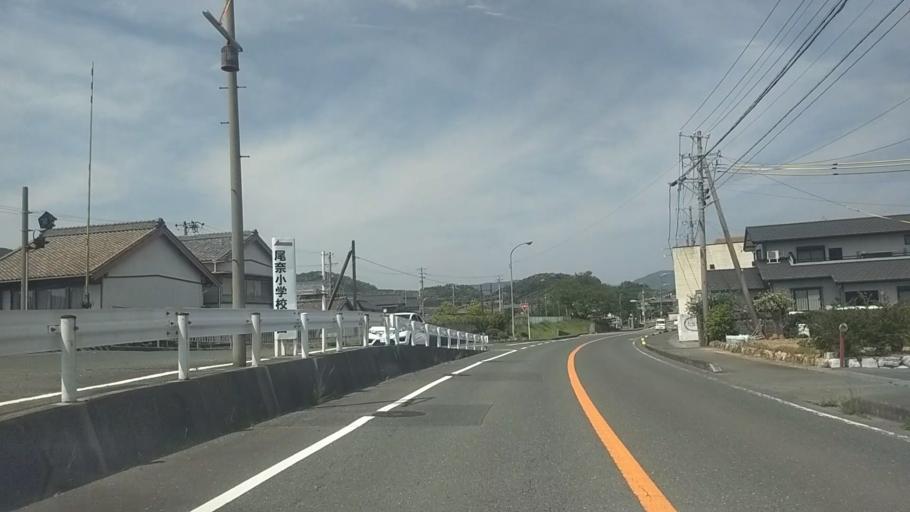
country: JP
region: Shizuoka
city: Kosai-shi
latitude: 34.7823
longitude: 137.5415
